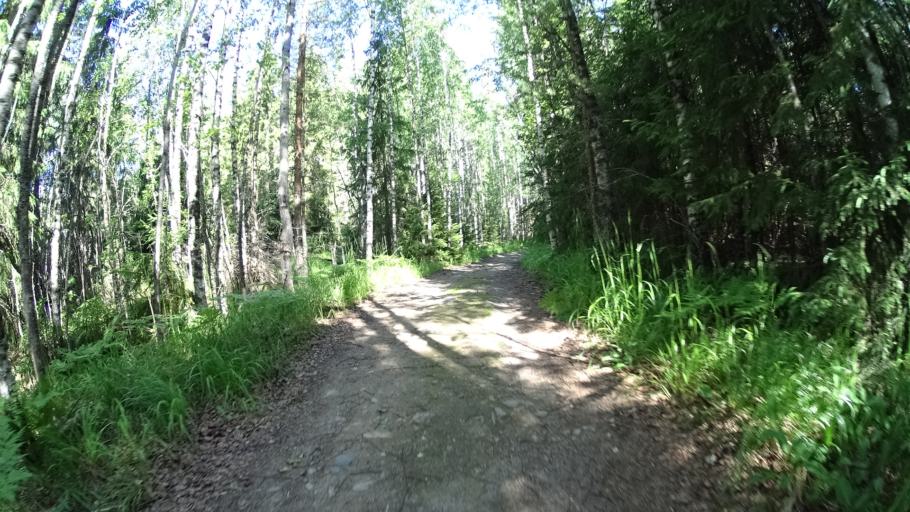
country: FI
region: Uusimaa
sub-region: Helsinki
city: Espoo
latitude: 60.3165
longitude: 24.5020
